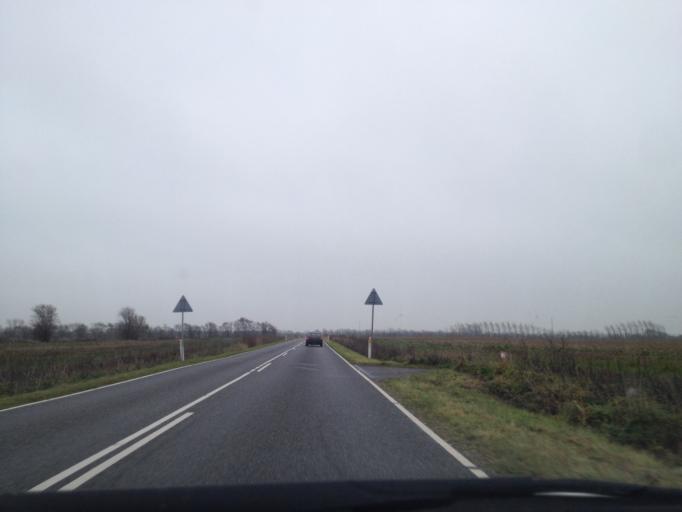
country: DK
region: South Denmark
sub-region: Tonder Kommune
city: Sherrebek
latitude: 55.0712
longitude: 8.7302
